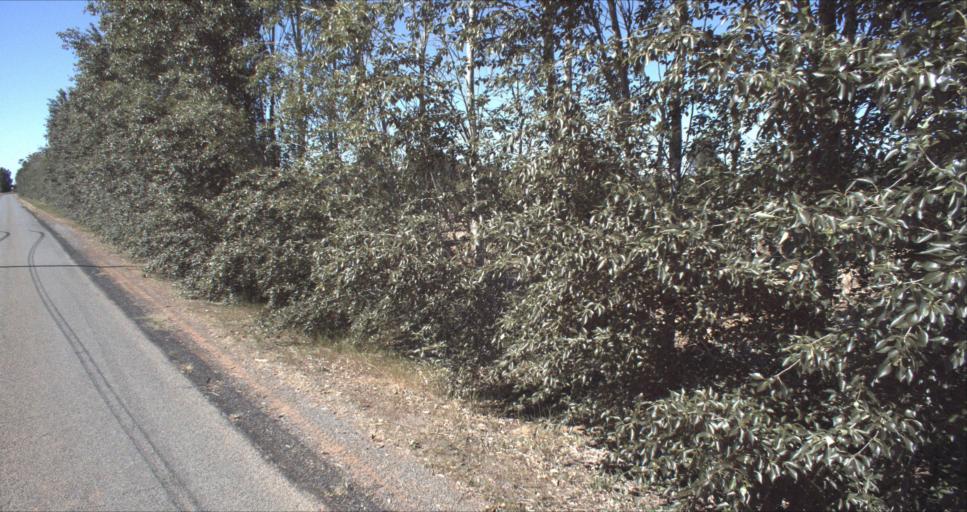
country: AU
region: New South Wales
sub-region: Leeton
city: Leeton
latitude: -34.5408
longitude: 146.3411
